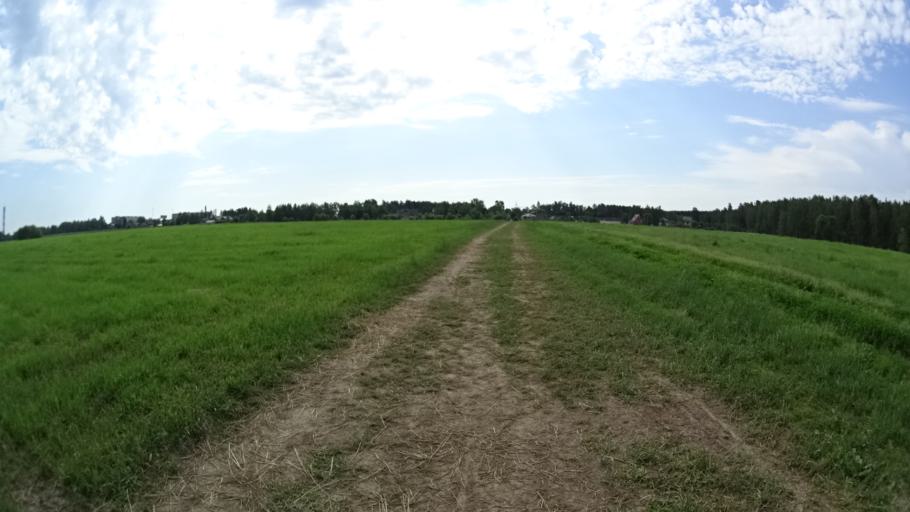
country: RU
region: Moskovskaya
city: Lesnoy
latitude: 56.0831
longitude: 37.9106
